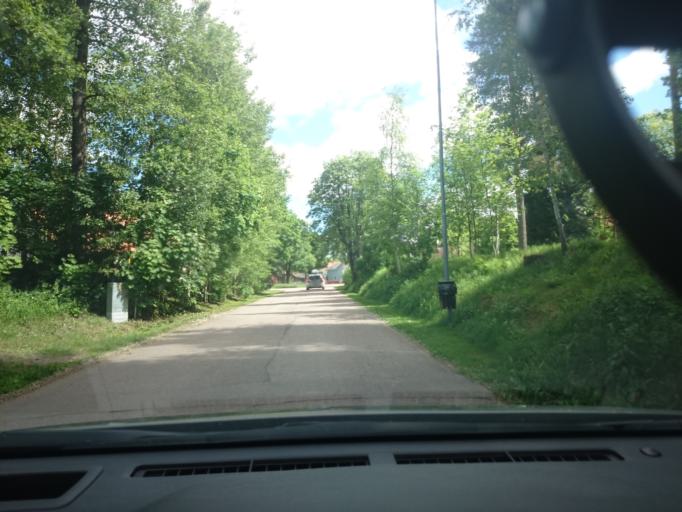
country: SE
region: Dalarna
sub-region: Saters Kommun
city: Saeter
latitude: 60.3898
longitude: 15.6668
